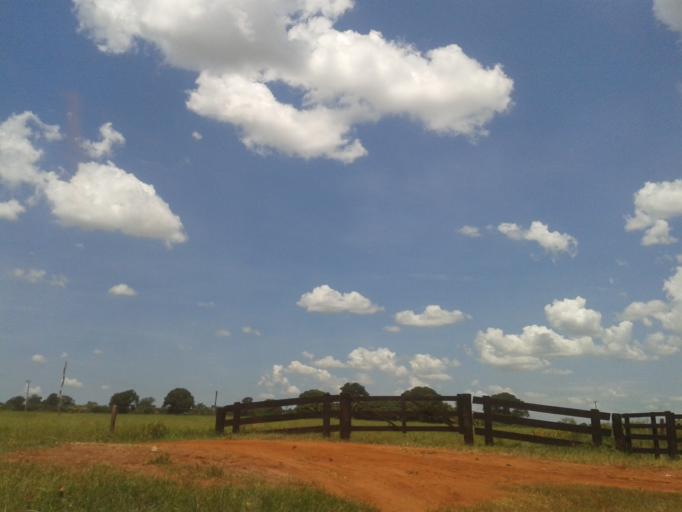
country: BR
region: Minas Gerais
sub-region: Santa Vitoria
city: Santa Vitoria
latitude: -19.2109
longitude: -50.4013
